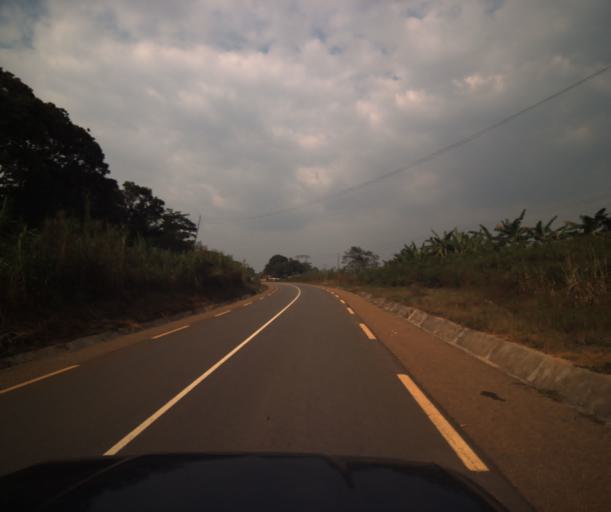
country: CM
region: Centre
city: Mbankomo
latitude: 3.7031
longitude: 11.3736
